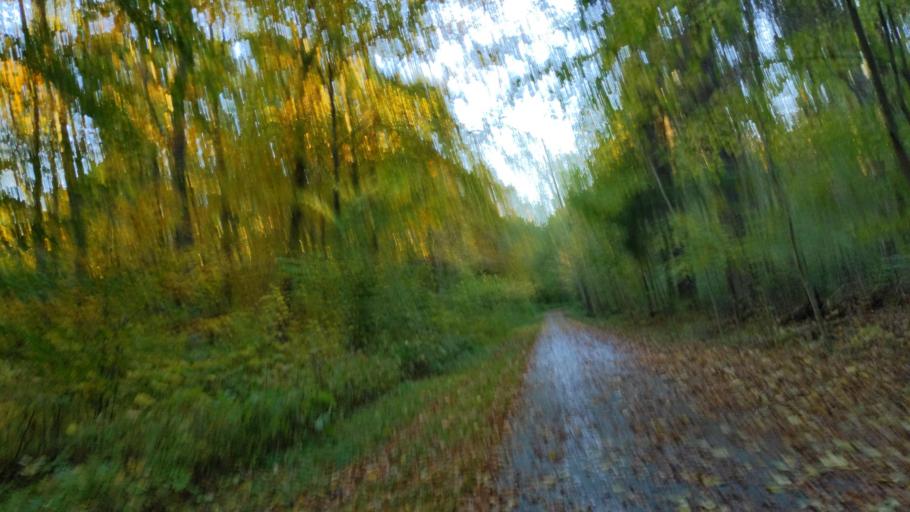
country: DE
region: Schleswig-Holstein
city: Bad Schwartau
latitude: 53.8916
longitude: 10.7510
